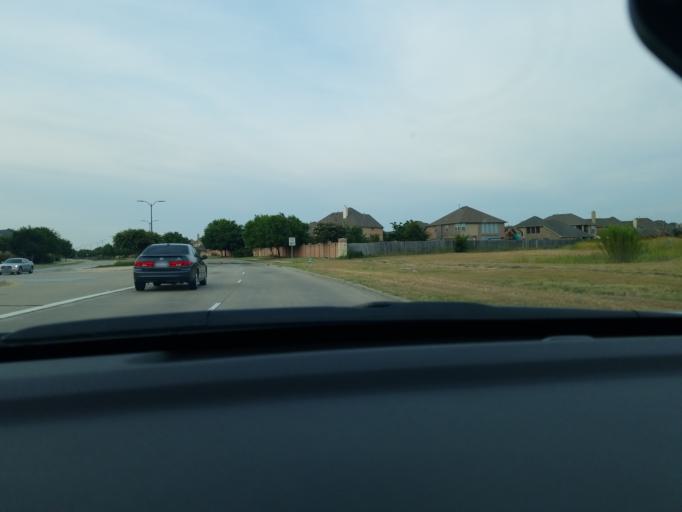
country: US
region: Texas
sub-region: Denton County
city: Little Elm
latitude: 33.1707
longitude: -96.8968
